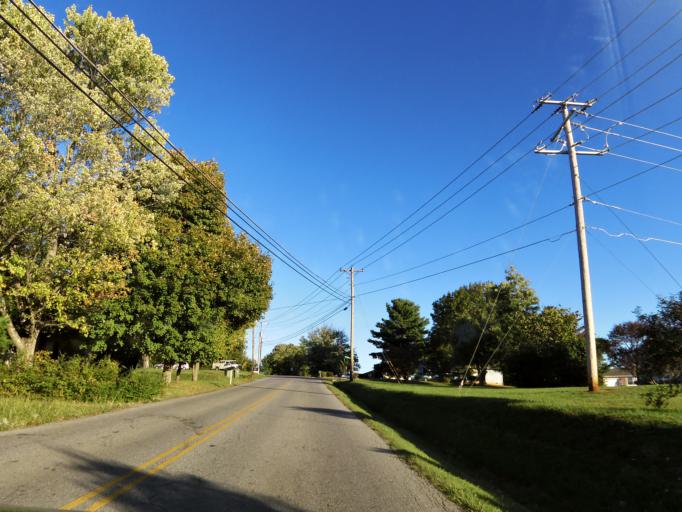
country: US
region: Tennessee
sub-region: Blount County
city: Eagleton Village
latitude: 35.7752
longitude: -83.9460
